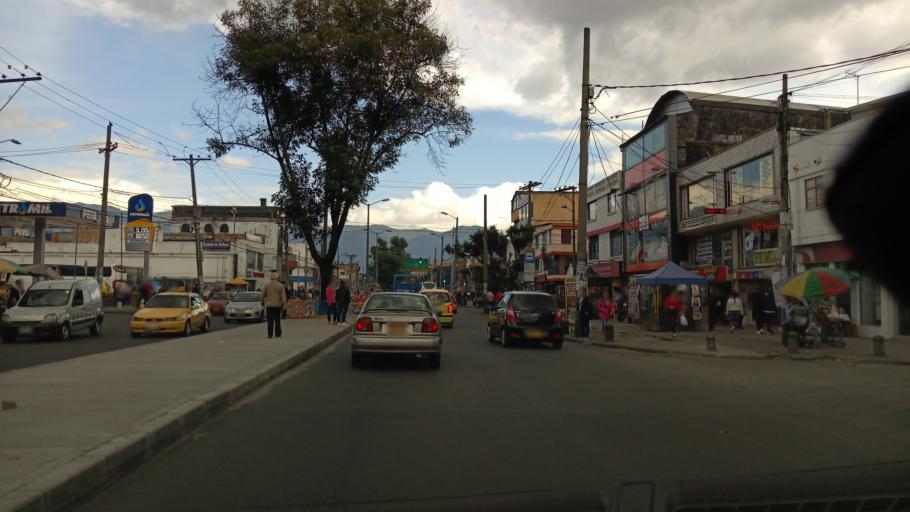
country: CO
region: Bogota D.C.
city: Barrio San Luis
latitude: 4.6814
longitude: -74.0893
